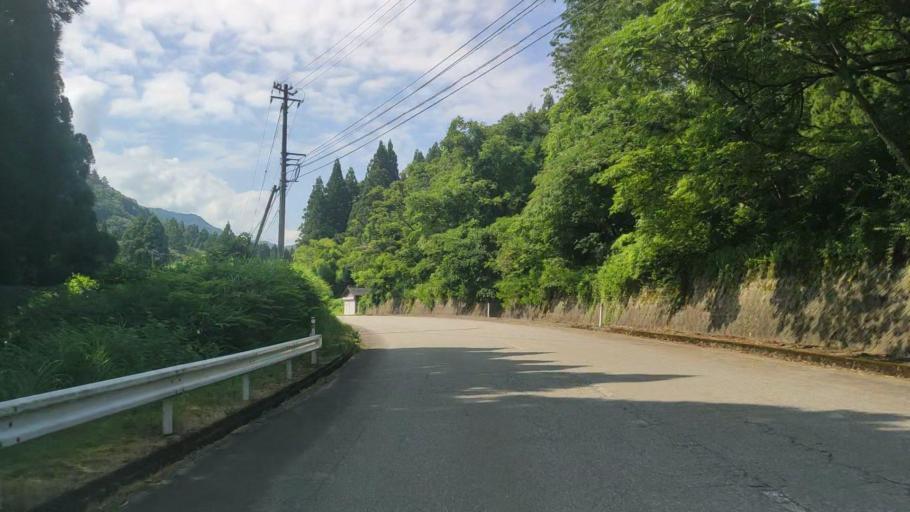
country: JP
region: Ishikawa
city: Komatsu
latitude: 36.3093
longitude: 136.5279
